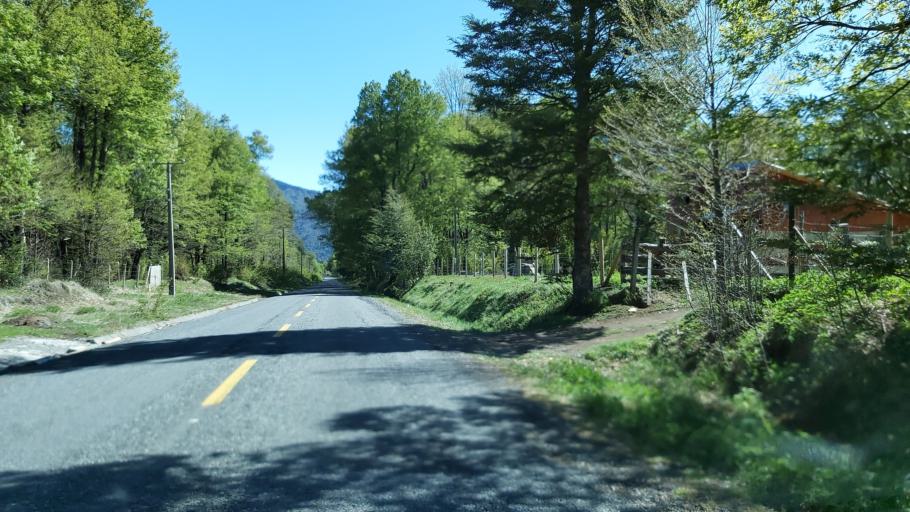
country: CL
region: Araucania
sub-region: Provincia de Cautin
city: Vilcun
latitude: -38.4693
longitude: -71.5231
